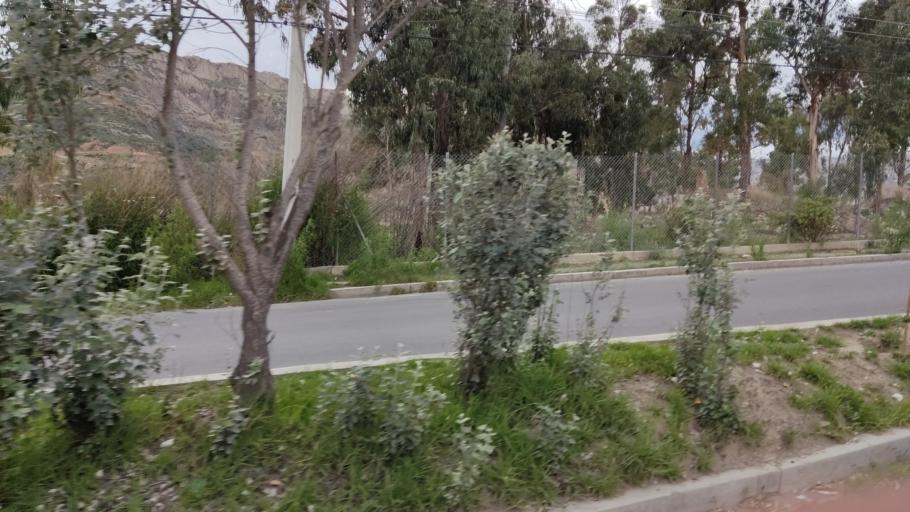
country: BO
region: La Paz
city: La Paz
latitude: -16.5807
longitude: -68.0800
